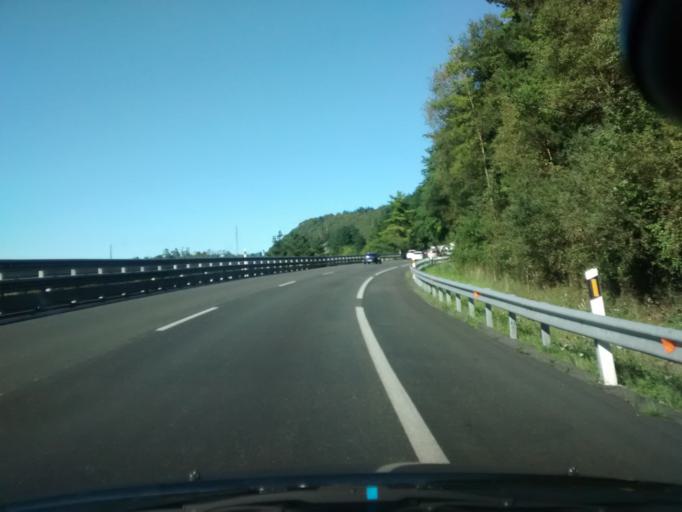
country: ES
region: Basque Country
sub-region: Provincia de Guipuzcoa
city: Mendaro
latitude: 43.2697
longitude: -2.3707
